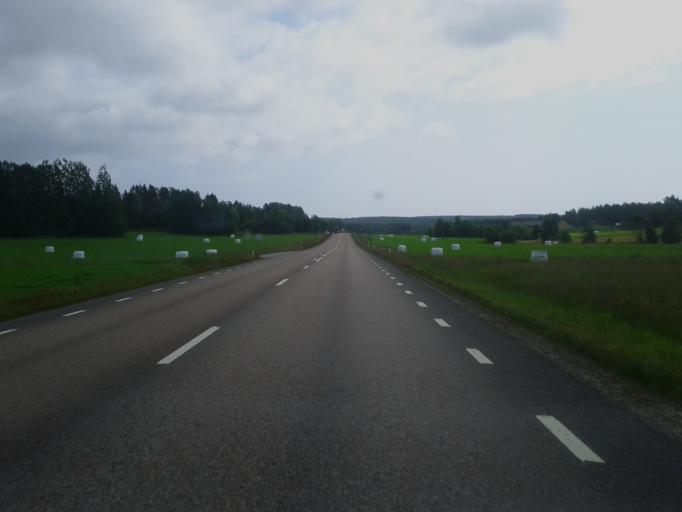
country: SE
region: Vaesterbotten
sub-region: Skelleftea Kommun
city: Burea
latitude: 64.3339
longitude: 21.2267
